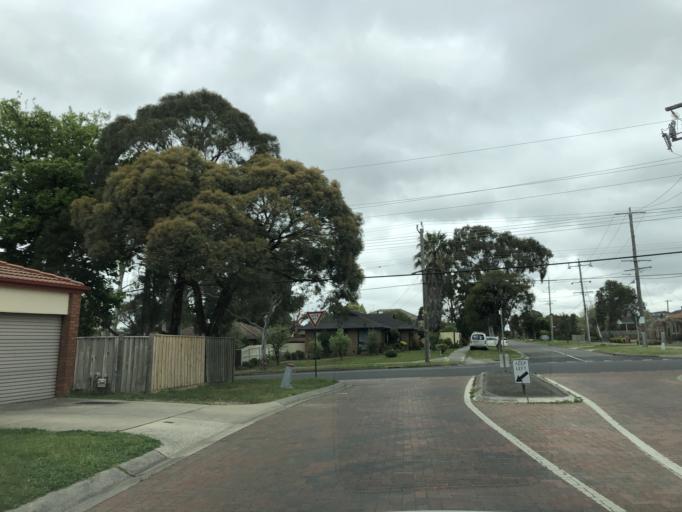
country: AU
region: Victoria
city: Burwood East
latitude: -37.8608
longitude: 145.1619
